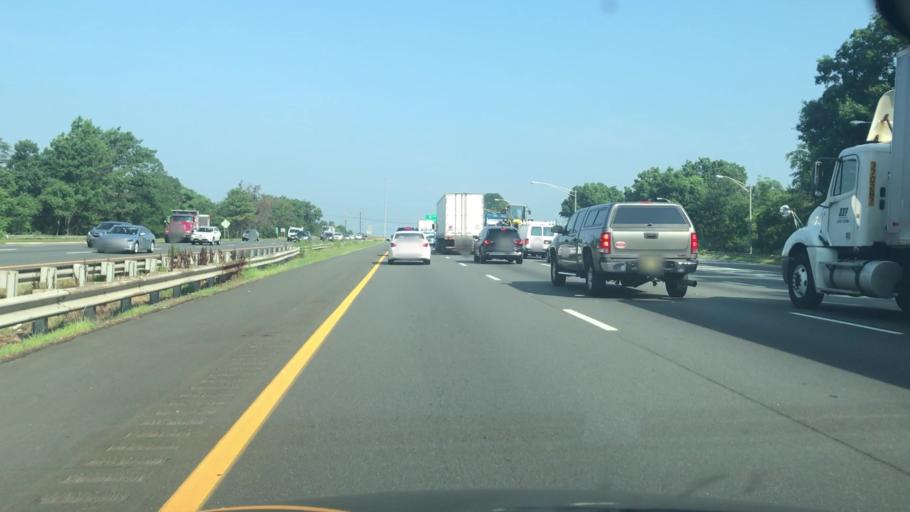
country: US
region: New Jersey
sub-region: Middlesex County
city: Metuchen
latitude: 40.5320
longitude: -74.3740
